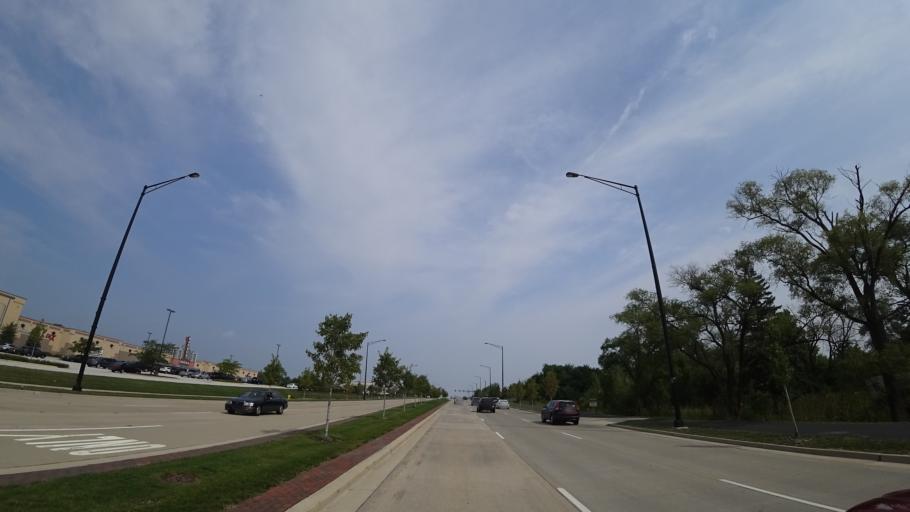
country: US
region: Illinois
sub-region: Cook County
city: Orland Hills
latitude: 41.5909
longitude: -87.8524
